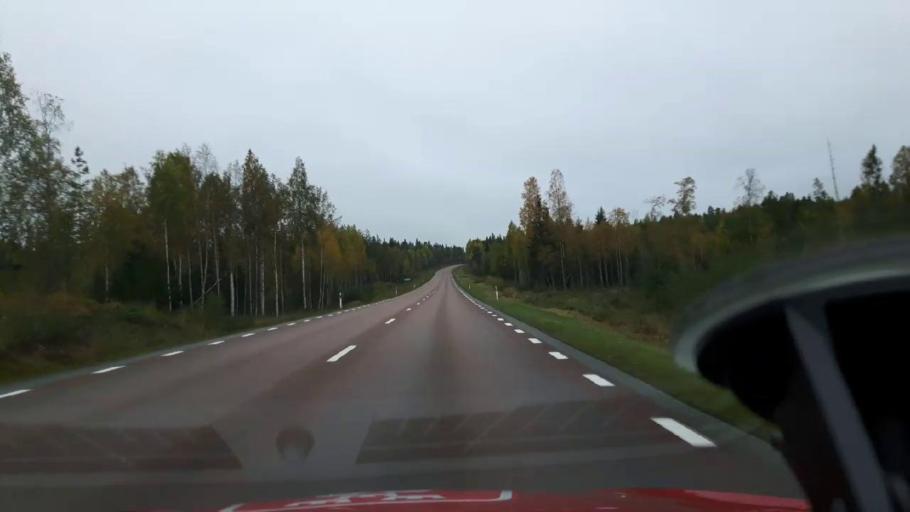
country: SE
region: Jaemtland
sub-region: Bergs Kommun
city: Hoverberg
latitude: 62.8374
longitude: 14.5196
